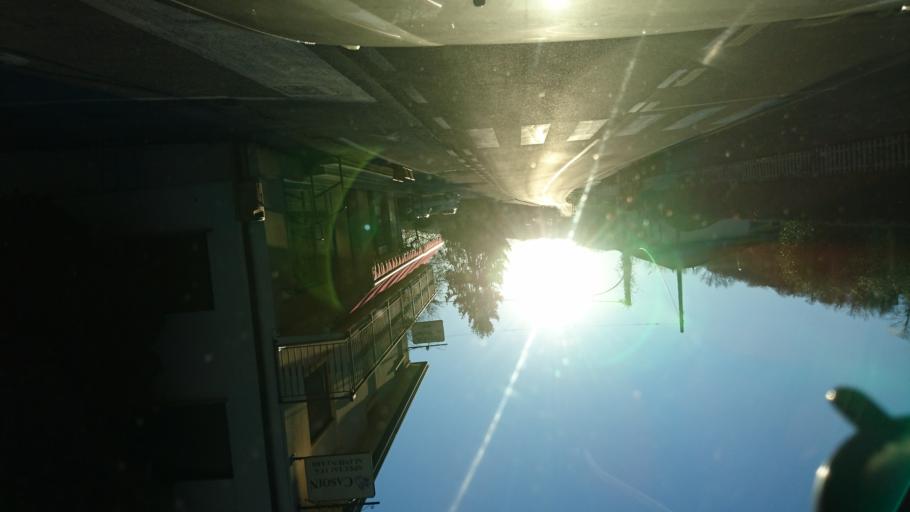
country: IT
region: Veneto
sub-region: Provincia di Treviso
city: Santa Maria
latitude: 45.9849
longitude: 12.2361
